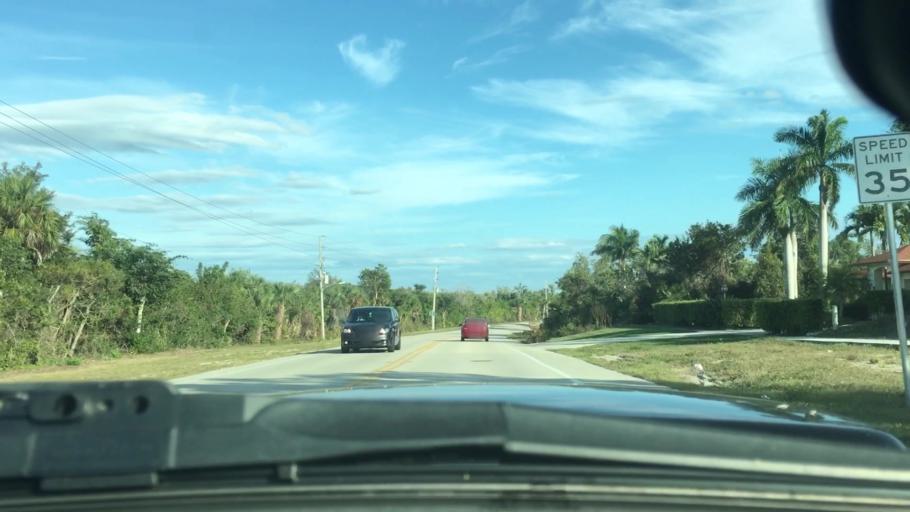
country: US
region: Florida
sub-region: Collier County
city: Marco
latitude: 25.9381
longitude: -81.6853
